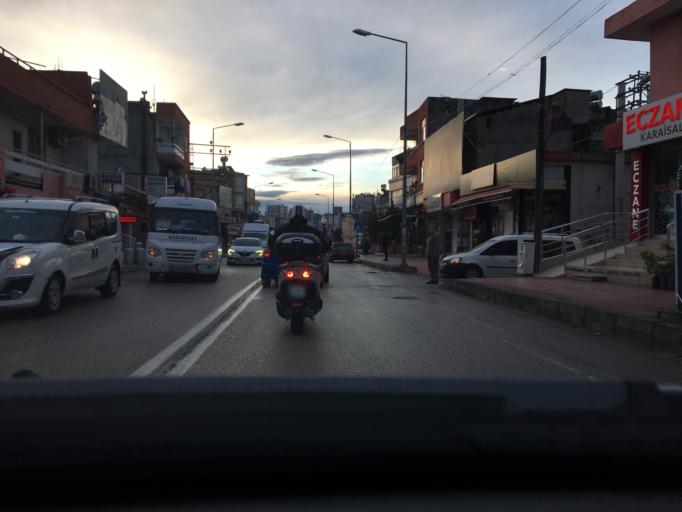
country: TR
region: Adana
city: Seyhan
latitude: 37.0198
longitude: 35.2960
